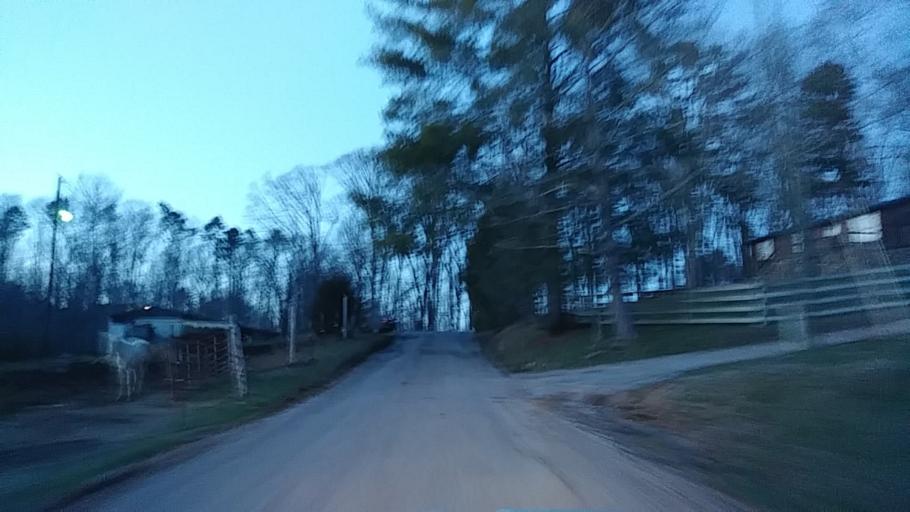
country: US
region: Tennessee
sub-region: Greene County
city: Mosheim
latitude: 36.0737
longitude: -82.9898
